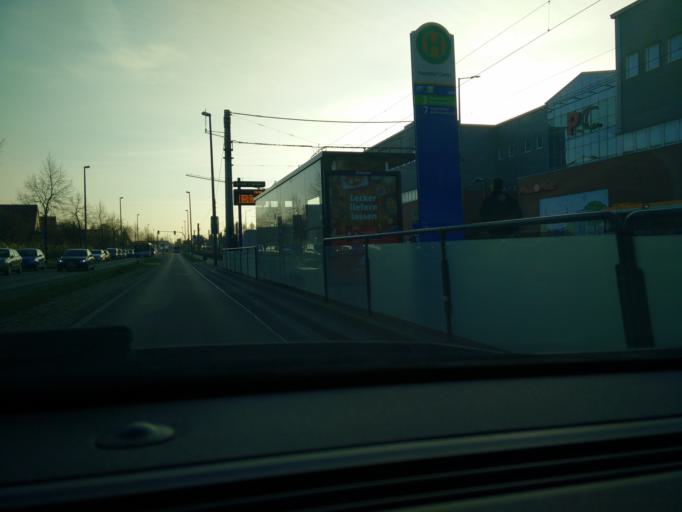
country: DE
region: Saxony
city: Taucha
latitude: 51.3491
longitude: 12.4793
